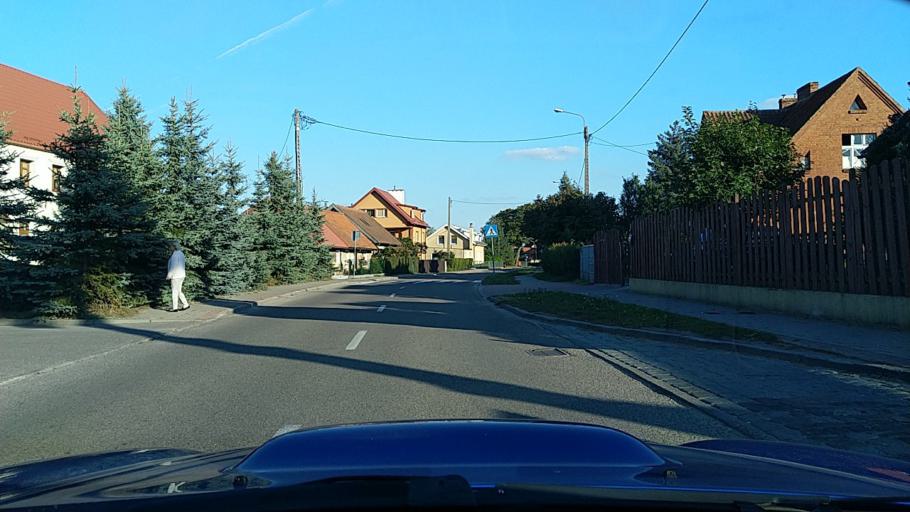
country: PL
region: Warmian-Masurian Voivodeship
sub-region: Olsztyn
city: Kortowo
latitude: 53.7683
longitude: 20.4197
